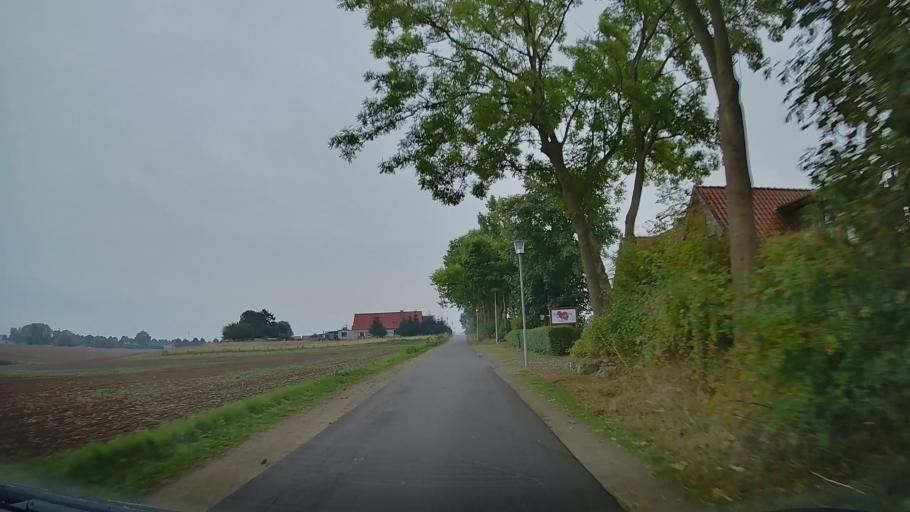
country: DE
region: Mecklenburg-Vorpommern
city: Klutz
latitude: 54.0027
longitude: 11.1637
